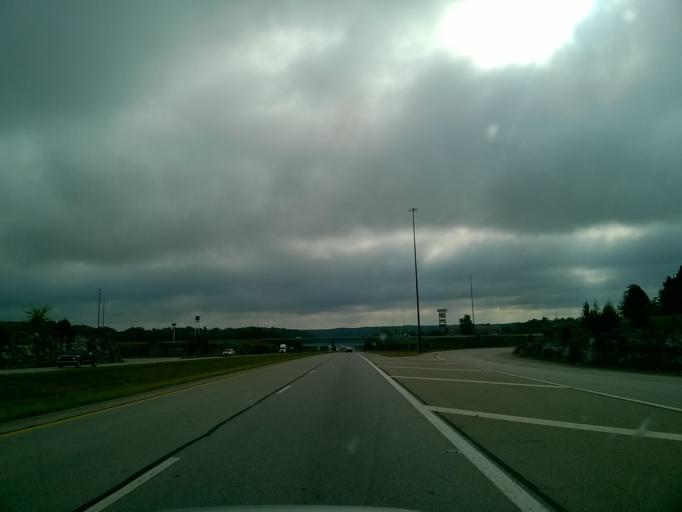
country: US
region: Indiana
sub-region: Harrison County
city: Corydon
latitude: 38.2392
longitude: -86.1305
